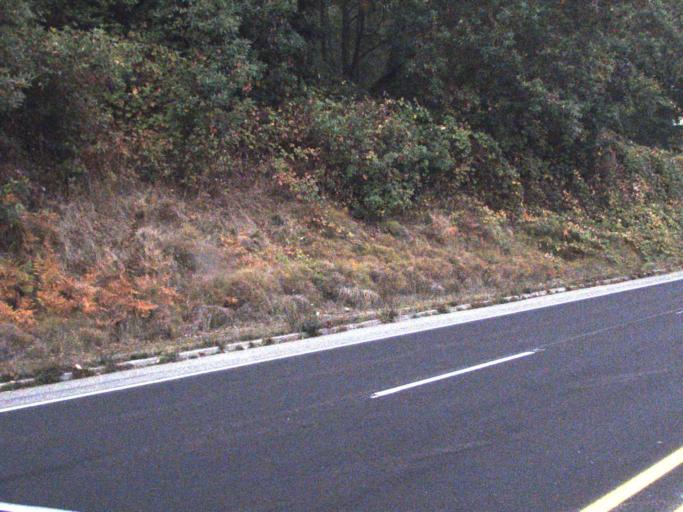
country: US
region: Washington
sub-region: Snohomish County
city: Mukilteo
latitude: 47.9795
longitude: -122.3667
